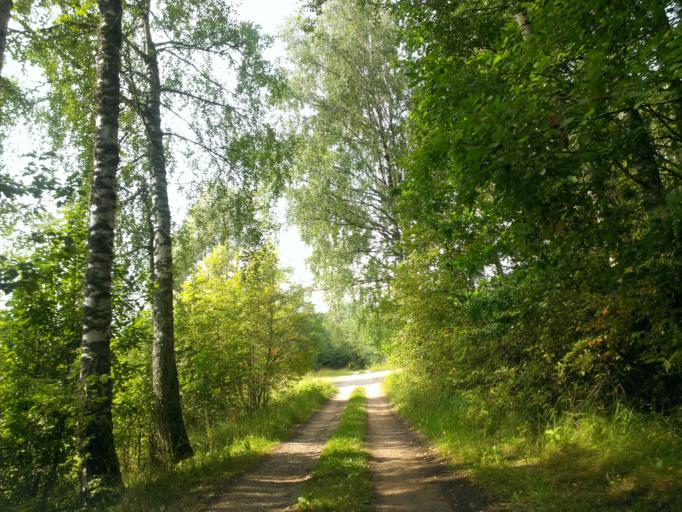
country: LV
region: Amatas Novads
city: Drabesi
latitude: 57.2445
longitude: 25.3124
